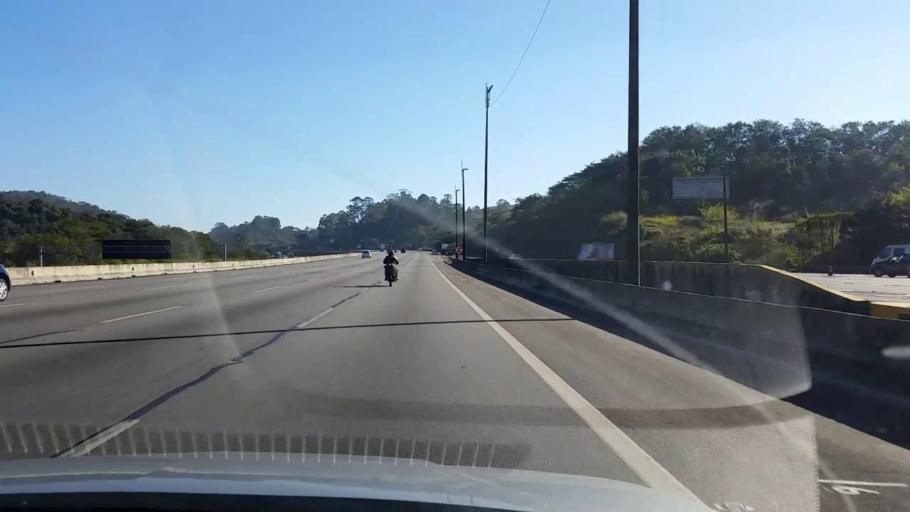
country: BR
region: Sao Paulo
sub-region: Caieiras
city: Caieiras
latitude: -23.4270
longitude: -46.7605
